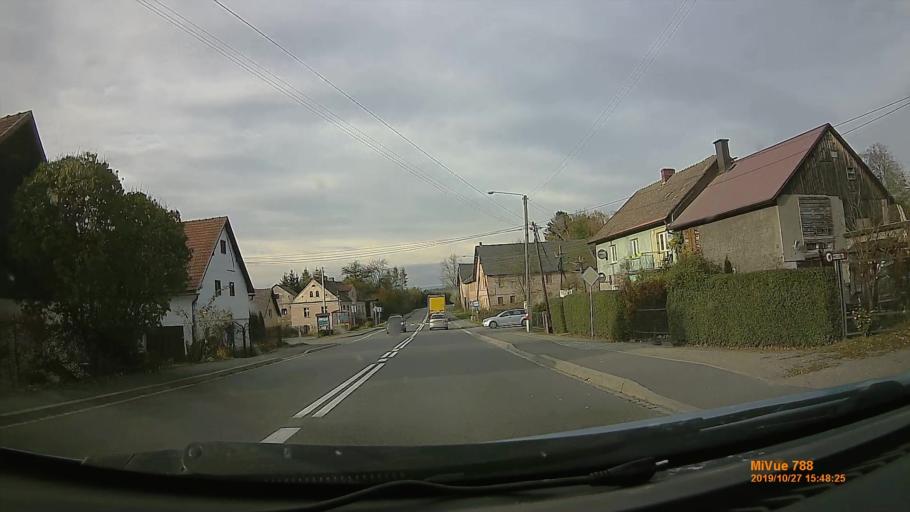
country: PL
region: Lower Silesian Voivodeship
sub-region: Powiat klodzki
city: Bozkow
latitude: 50.4973
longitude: 16.5862
